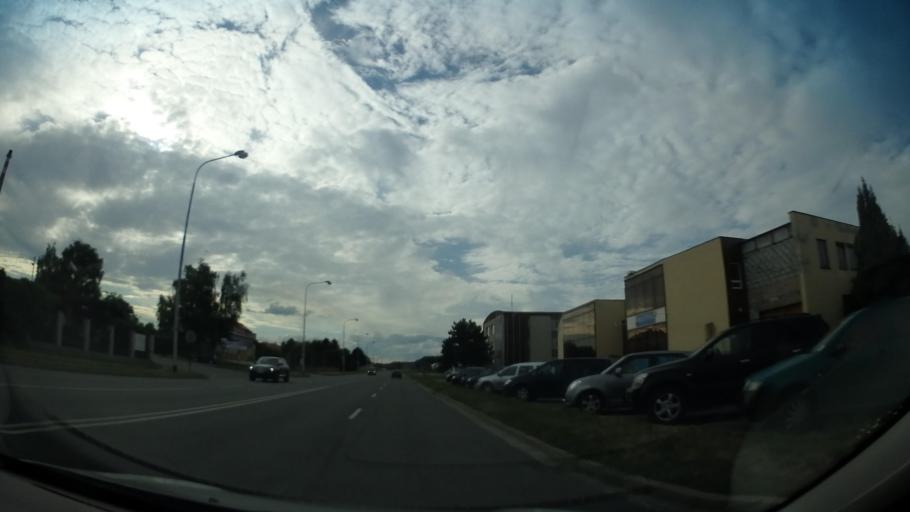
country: CZ
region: Zlin
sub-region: Okres Kromeriz
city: Kromeriz
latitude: 49.3086
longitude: 17.4011
